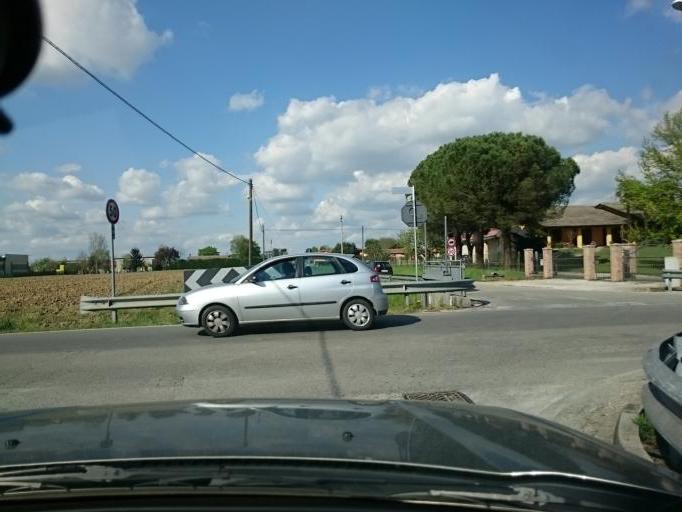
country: IT
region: Veneto
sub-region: Provincia di Venezia
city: Sant'Angelo
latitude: 45.5195
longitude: 12.0261
